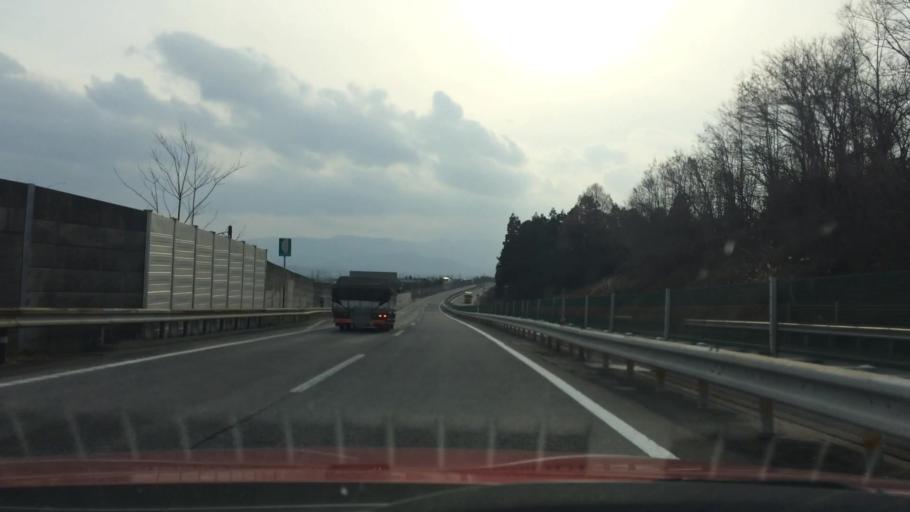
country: JP
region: Nagano
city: Iida
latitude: 35.5384
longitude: 137.8367
